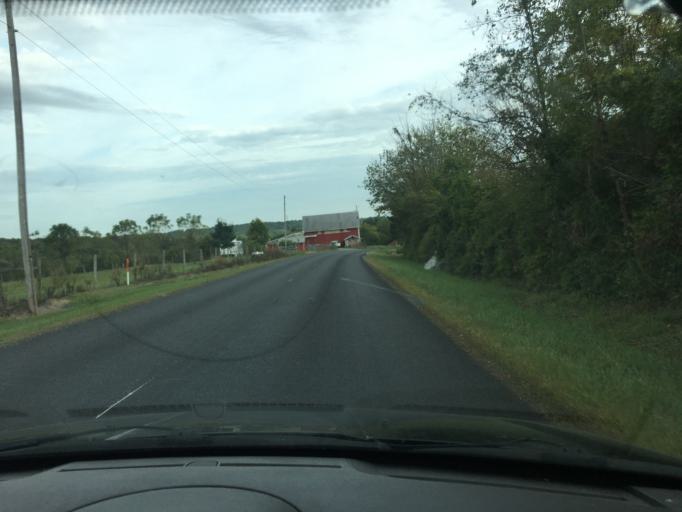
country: US
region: Ohio
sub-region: Logan County
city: Bellefontaine
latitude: 40.3165
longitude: -83.7134
